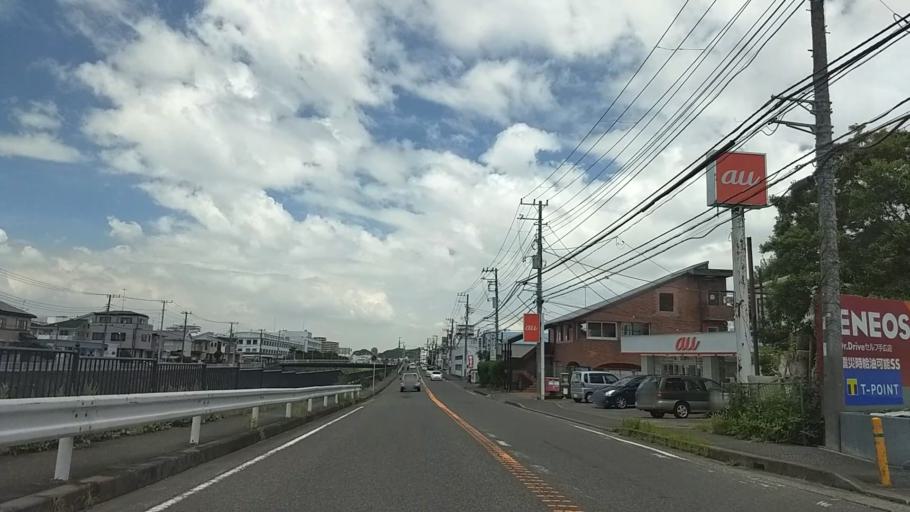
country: JP
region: Kanagawa
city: Fujisawa
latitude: 35.3341
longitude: 139.5106
